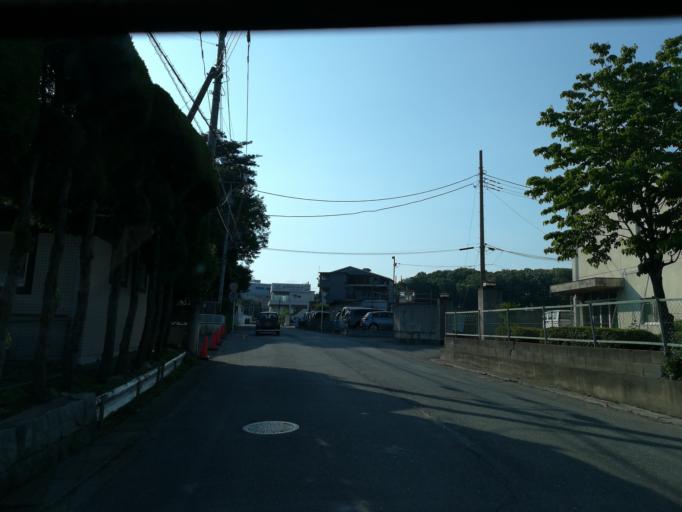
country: JP
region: Saitama
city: Sayama
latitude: 35.8041
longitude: 139.3825
